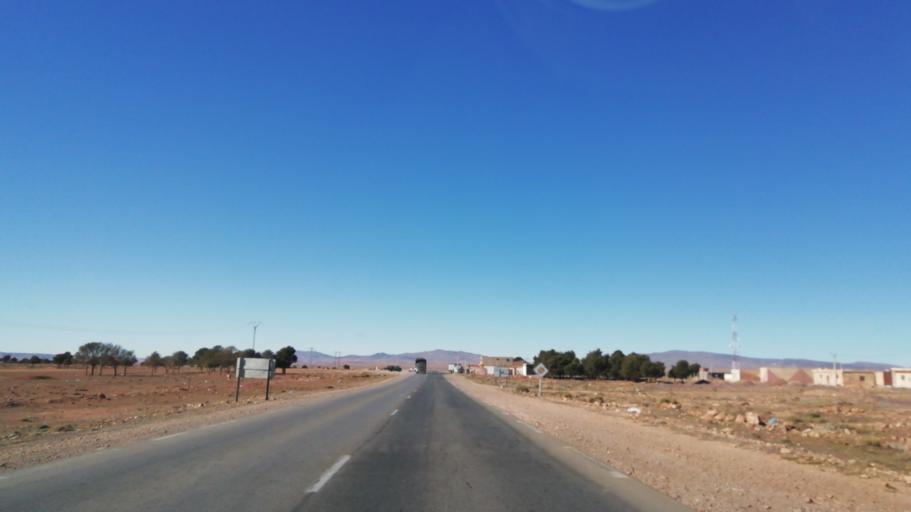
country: DZ
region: El Bayadh
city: El Bayadh
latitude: 33.6325
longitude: 1.3552
